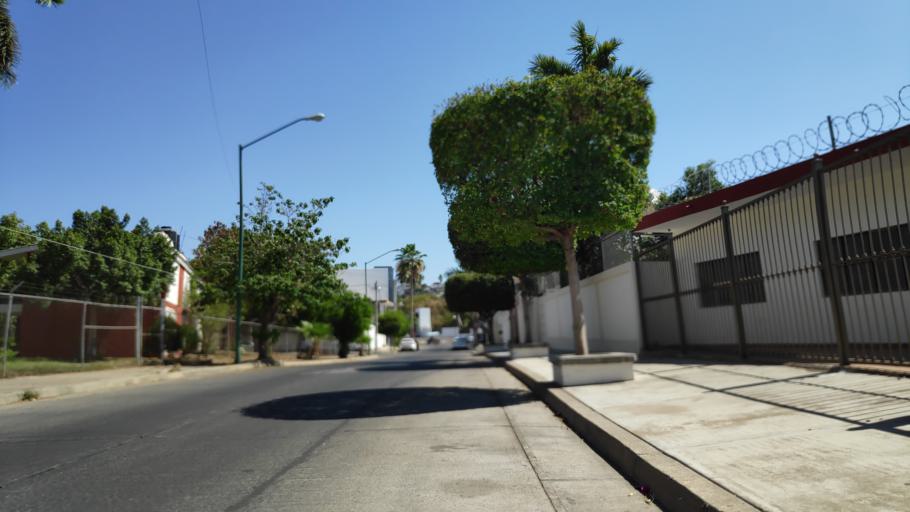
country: MX
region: Sinaloa
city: Culiacan
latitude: 24.7905
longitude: -107.3989
